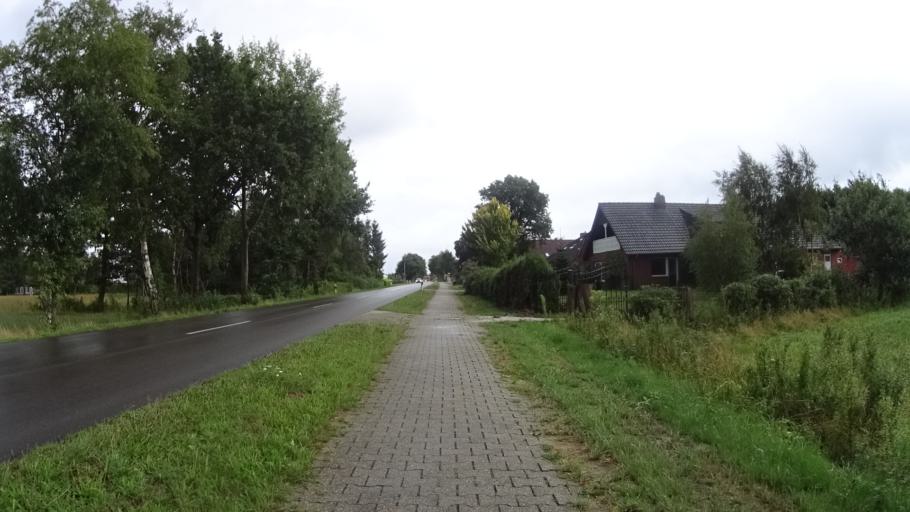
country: DE
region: Lower Saxony
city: Schwerinsdorf
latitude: 53.3457
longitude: 7.7368
